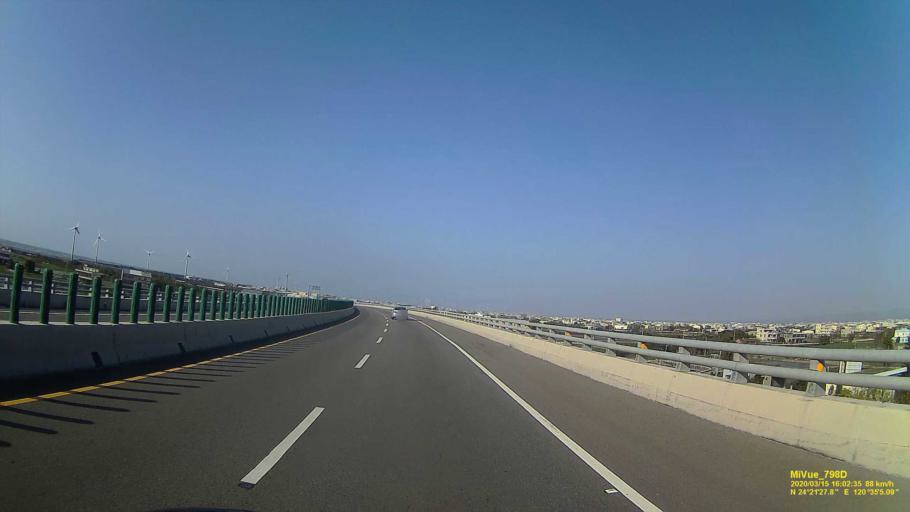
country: TW
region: Taiwan
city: Fengyuan
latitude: 24.3647
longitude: 120.5824
